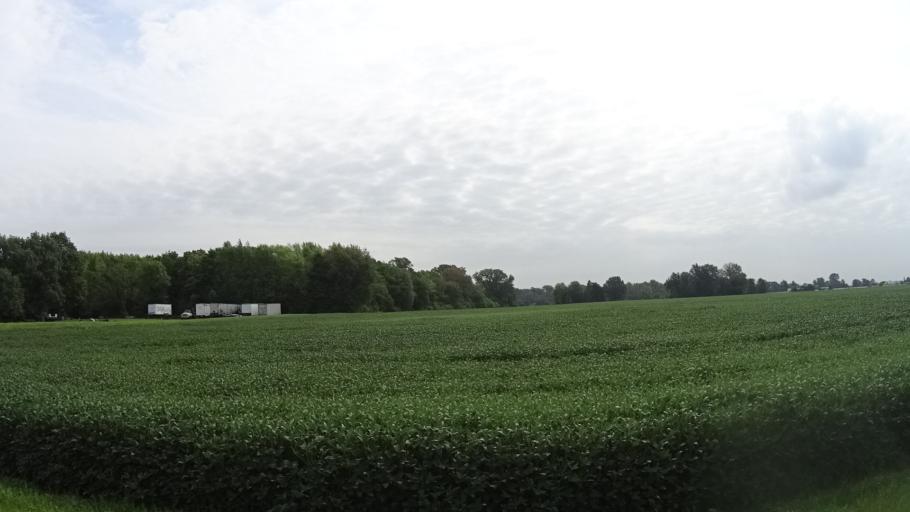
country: US
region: Indiana
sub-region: Madison County
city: Pendleton
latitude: 39.9973
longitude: -85.7870
